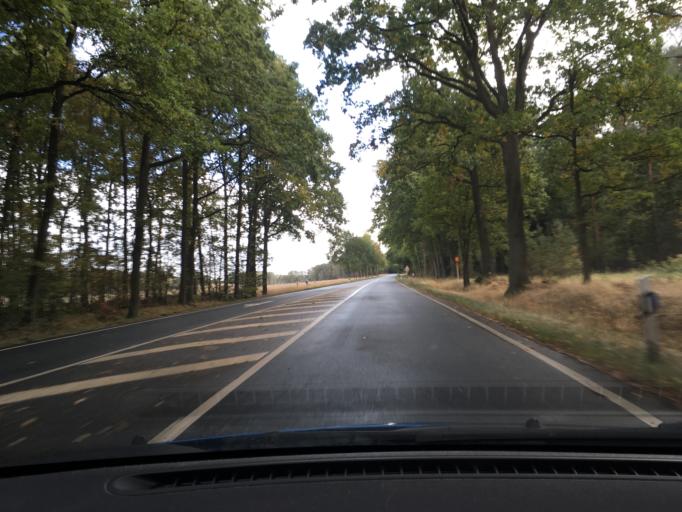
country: DE
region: Lower Saxony
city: Schnega
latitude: 52.9209
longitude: 10.8706
